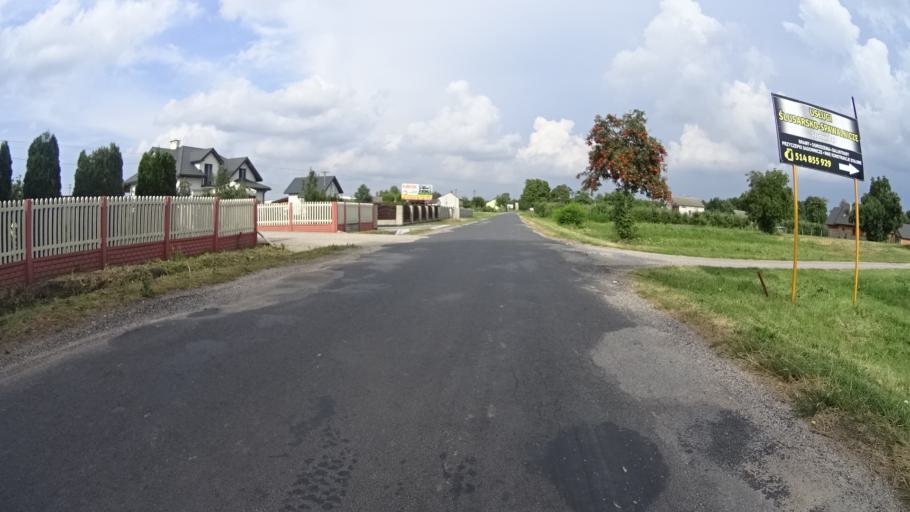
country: PL
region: Masovian Voivodeship
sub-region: Powiat grojecki
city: Goszczyn
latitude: 51.7004
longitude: 20.8444
